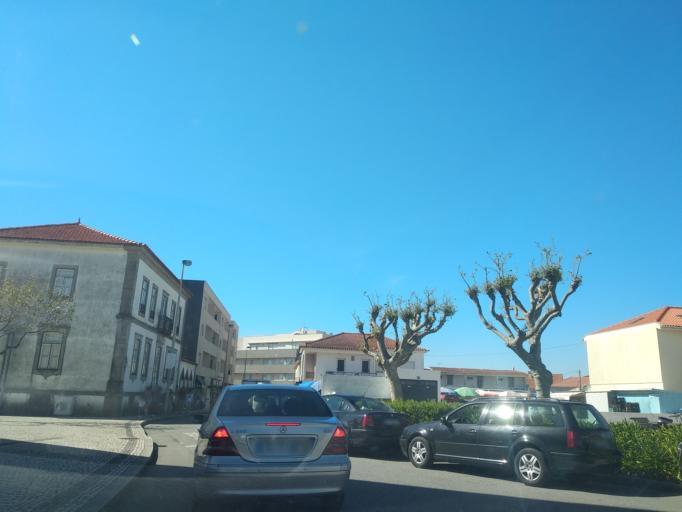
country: PT
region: Braga
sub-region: Esposende
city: Apulia
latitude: 41.4848
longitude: -8.7776
